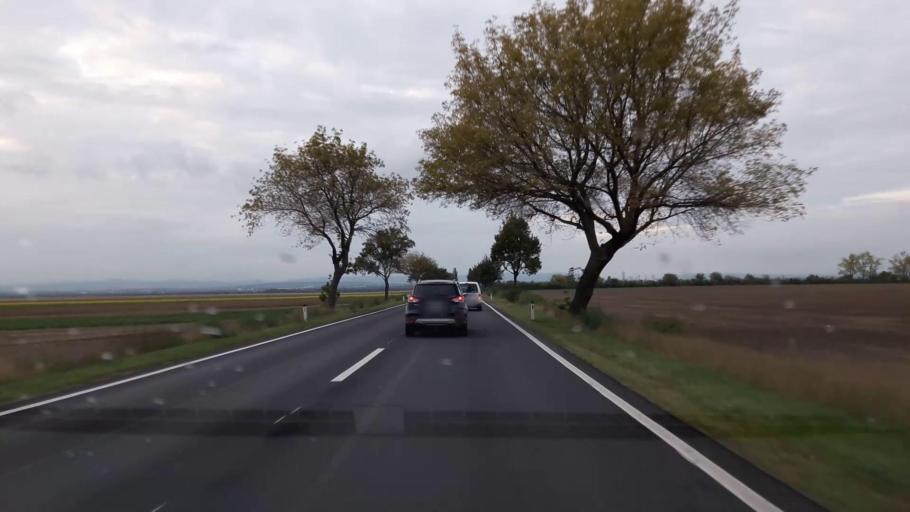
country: AT
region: Lower Austria
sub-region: Politischer Bezirk Wien-Umgebung
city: Rauchenwarth
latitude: 48.0924
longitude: 16.5494
